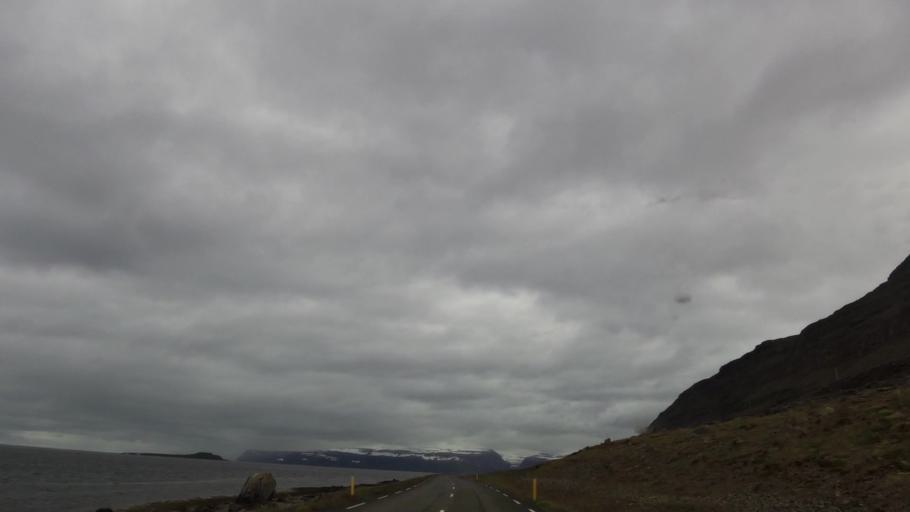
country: IS
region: Westfjords
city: Isafjoerdur
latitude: 66.0142
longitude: -22.7816
